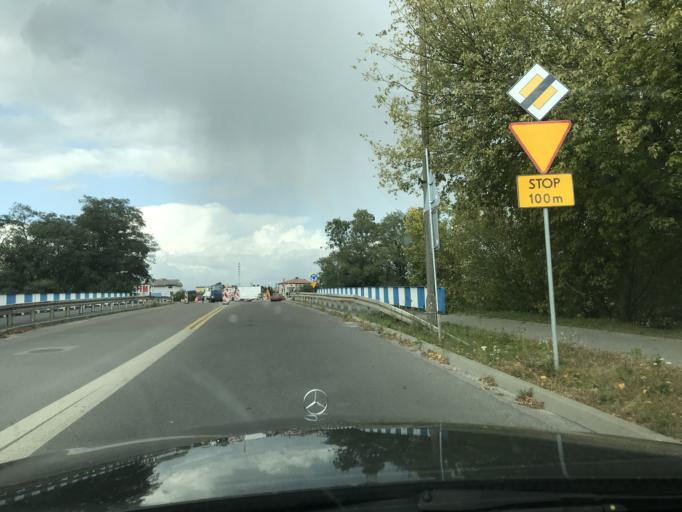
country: PL
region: Lublin Voivodeship
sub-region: Powiat lubartowski
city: Lubartow
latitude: 51.4729
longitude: 22.6063
